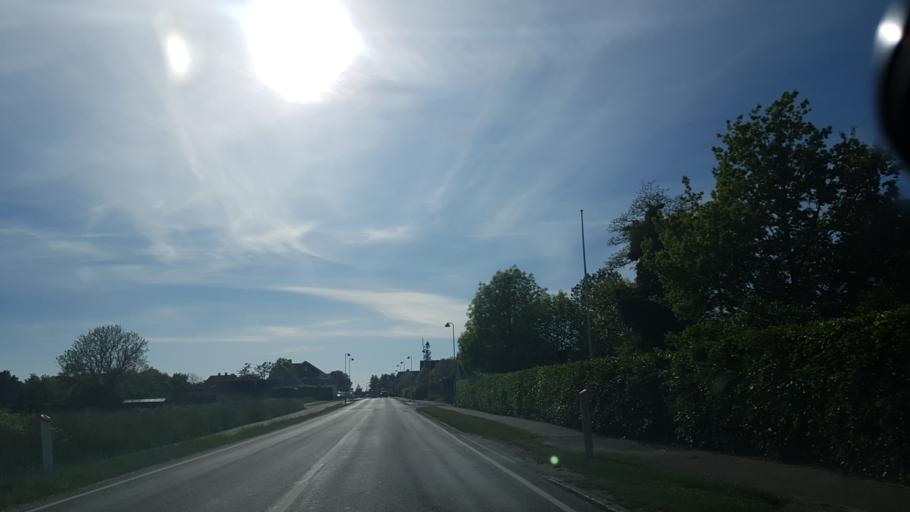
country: DK
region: Zealand
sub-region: Slagelse Kommune
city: Forlev
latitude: 55.4371
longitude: 11.2518
